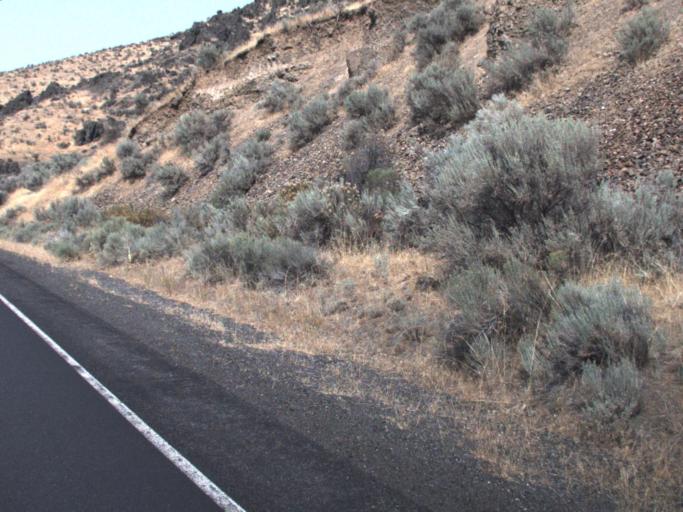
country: US
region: Washington
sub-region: Yakima County
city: Selah
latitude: 46.8060
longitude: -120.4402
